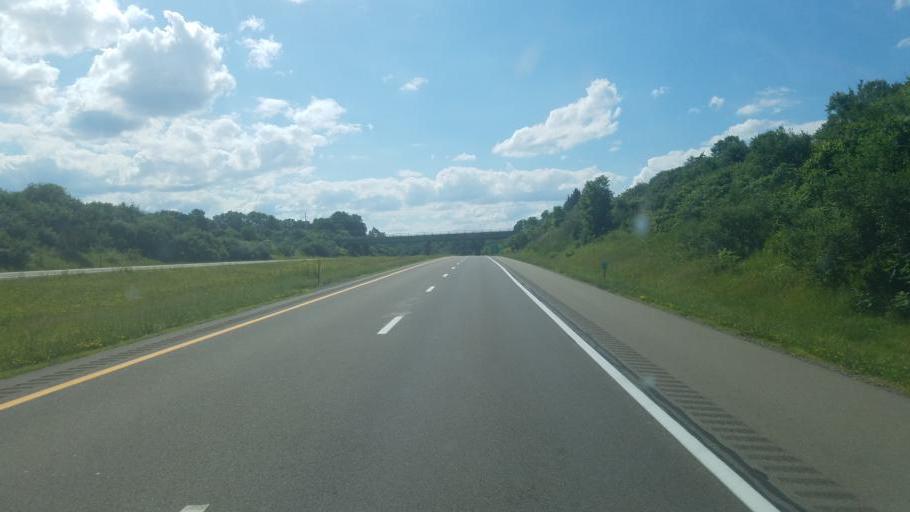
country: US
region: New York
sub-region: Steuben County
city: Hornell
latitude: 42.3783
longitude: -77.6512
